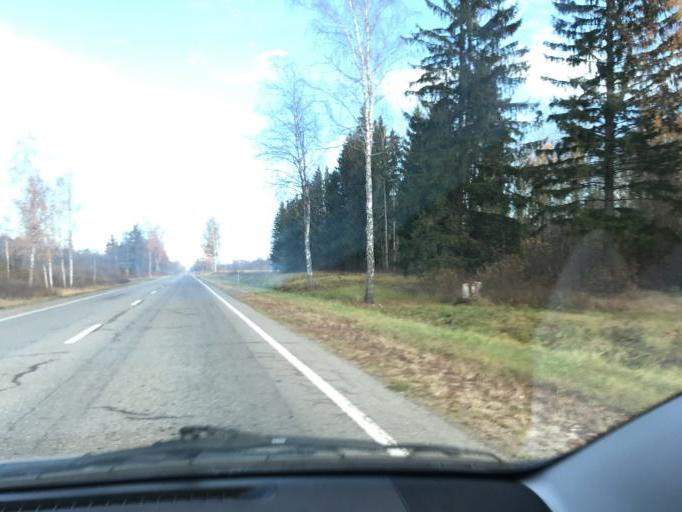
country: BY
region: Vitebsk
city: Haradok
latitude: 55.5167
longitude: 29.9706
